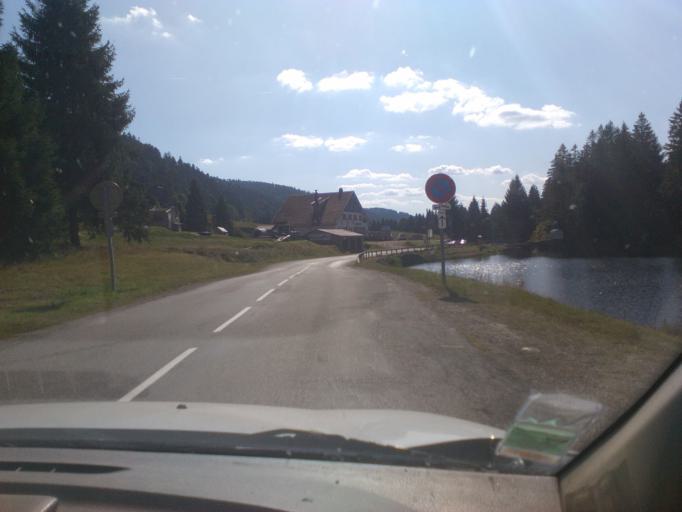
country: FR
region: Lorraine
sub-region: Departement des Vosges
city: Xonrupt-Longemer
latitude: 48.0407
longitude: 6.9313
